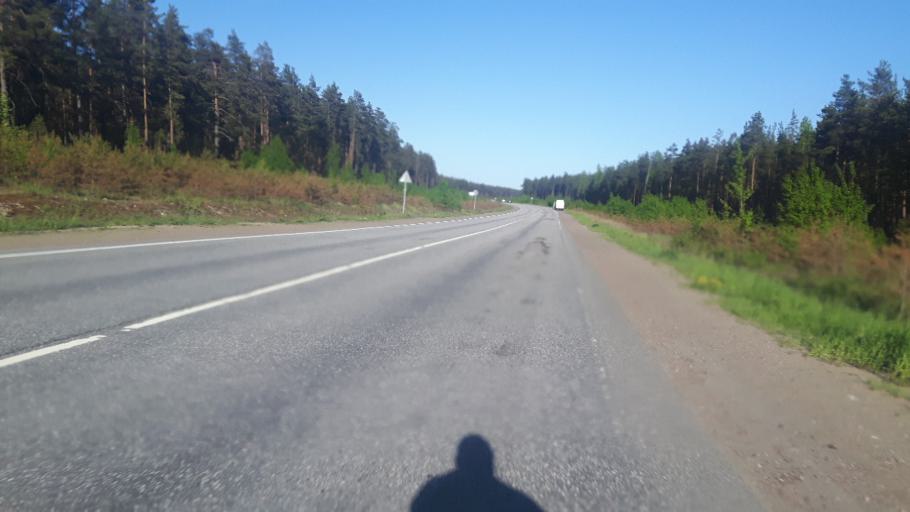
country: RU
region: Leningrad
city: Lebyazh'ye
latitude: 60.1682
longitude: 29.2255
